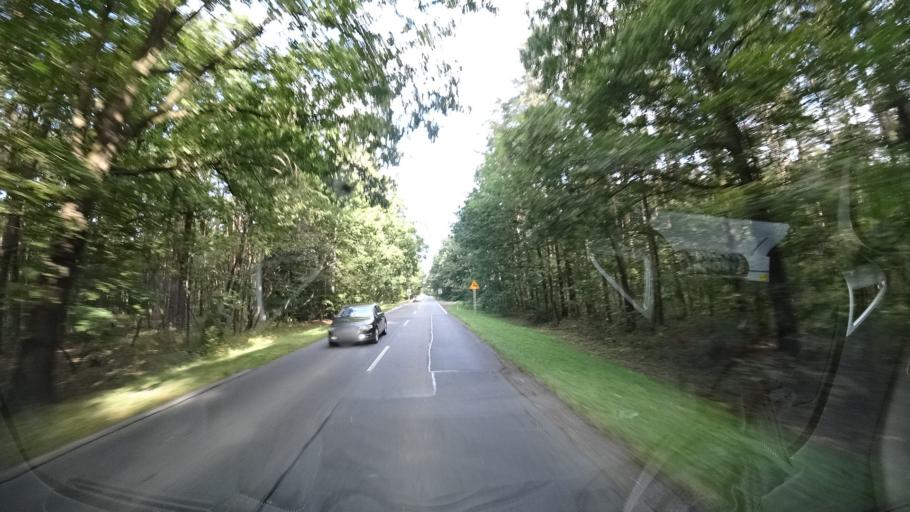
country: PL
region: Silesian Voivodeship
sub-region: Powiat raciborski
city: Rudy
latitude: 50.2683
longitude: 18.4287
